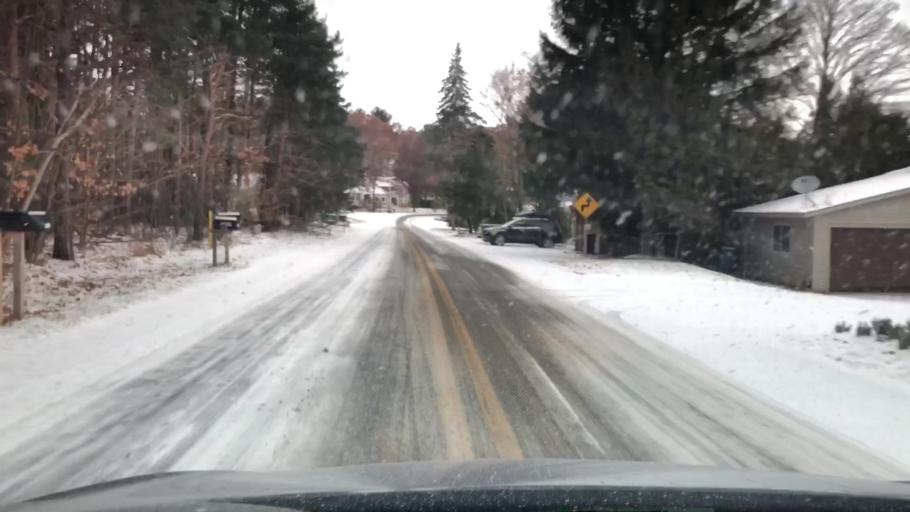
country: US
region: Michigan
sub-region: Grand Traverse County
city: Traverse City
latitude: 44.7993
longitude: -85.5608
